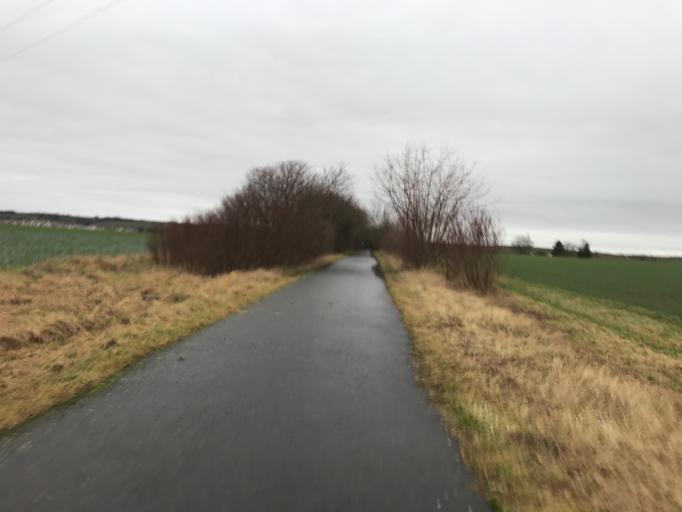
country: DE
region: Rheinland-Pfalz
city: Mommenheim
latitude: 49.8908
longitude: 8.2783
